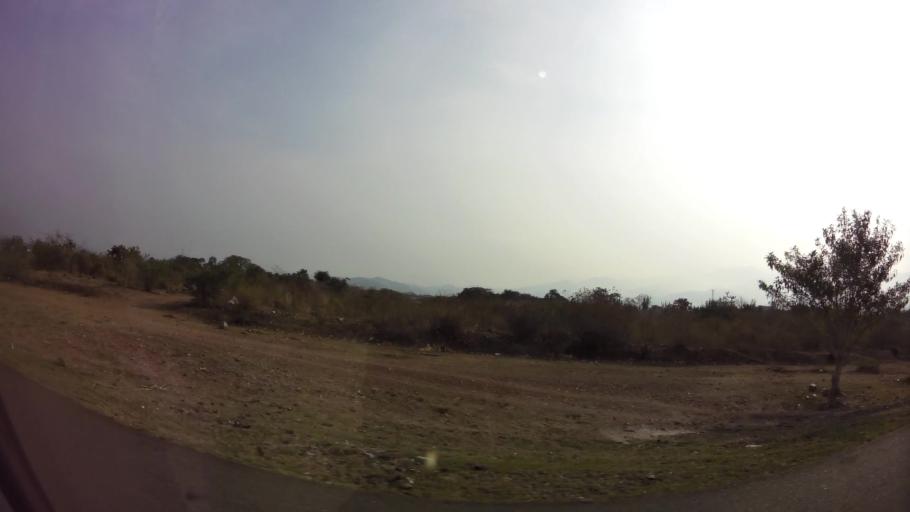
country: HN
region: Comayagua
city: Comayagua
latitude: 14.4289
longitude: -87.6409
